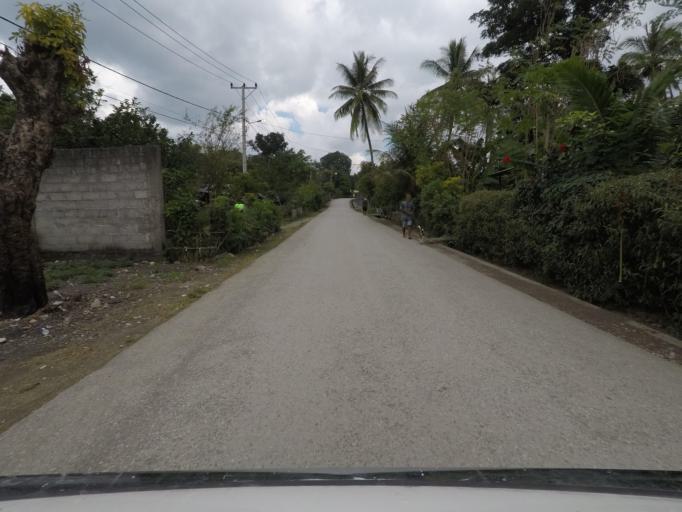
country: TL
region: Viqueque
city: Viqueque
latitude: -8.8683
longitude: 126.3675
